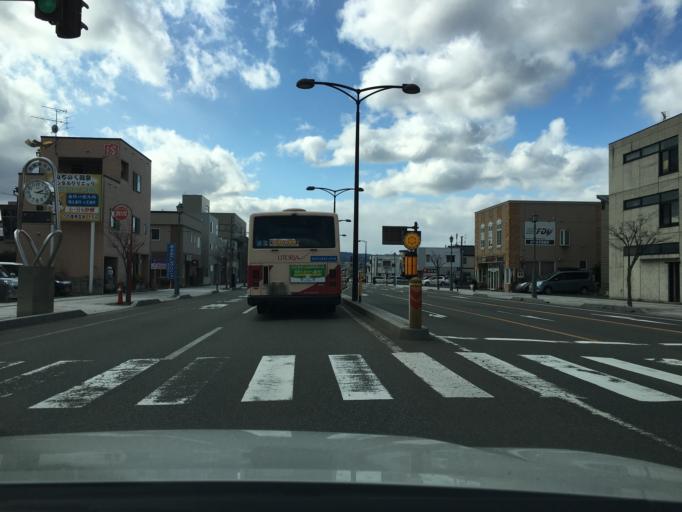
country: JP
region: Yamagata
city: Yamagata-shi
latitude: 38.2524
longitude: 140.3240
